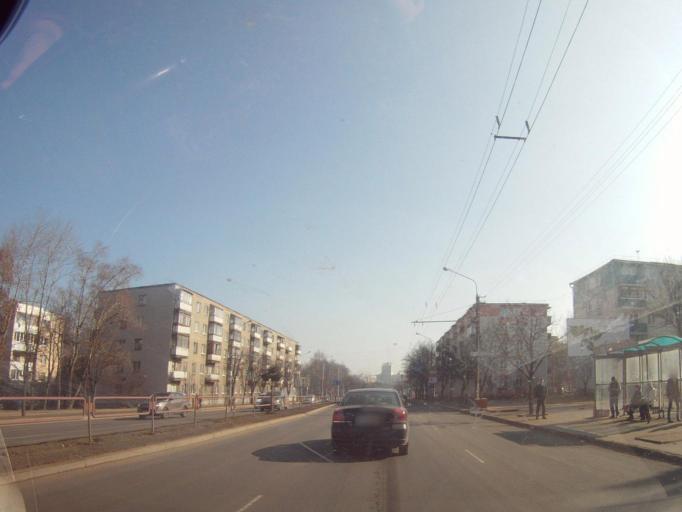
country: BY
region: Minsk
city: Minsk
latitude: 53.9321
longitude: 27.5634
